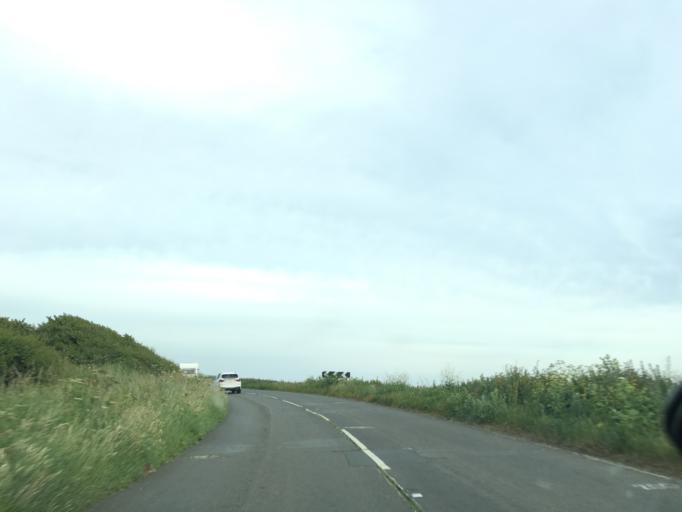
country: GB
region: England
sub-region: Isle of Wight
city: Shalfleet
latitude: 50.6401
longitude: -1.4264
